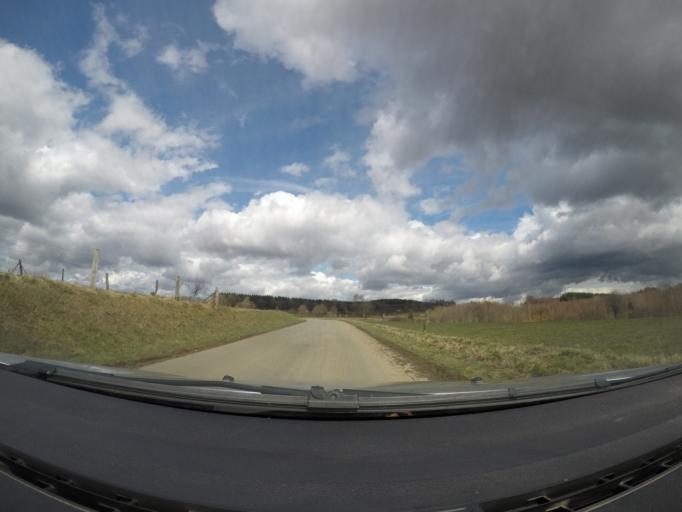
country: BE
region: Wallonia
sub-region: Province du Luxembourg
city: Leglise
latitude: 49.7741
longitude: 5.5250
